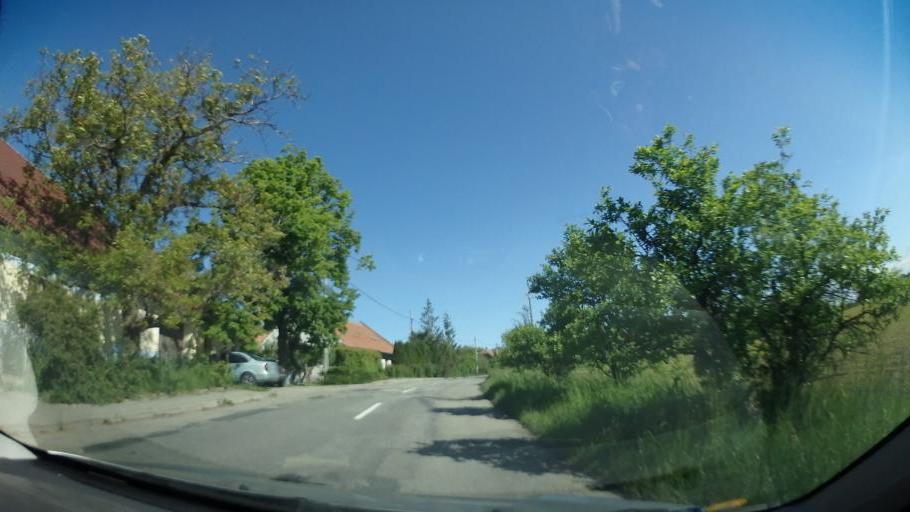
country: CZ
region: South Moravian
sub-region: Okres Blansko
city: Letovice
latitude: 49.5914
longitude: 16.5952
